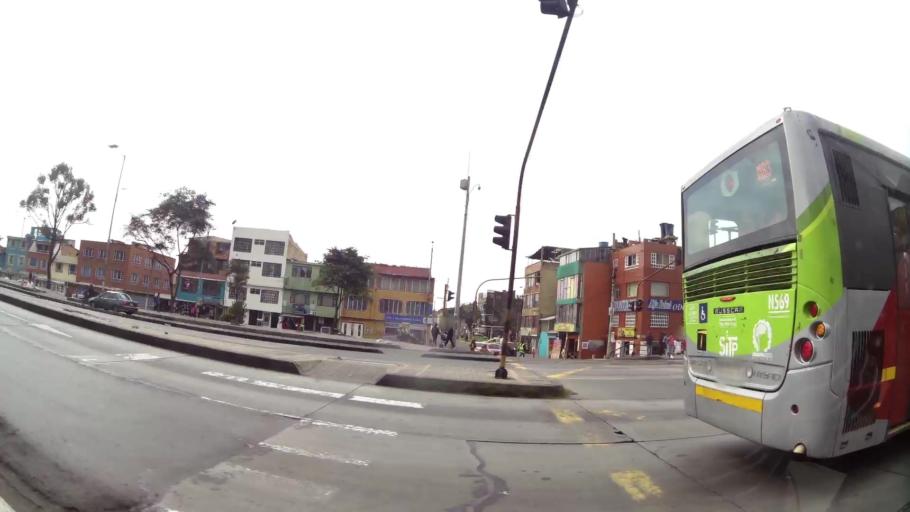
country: CO
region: Bogota D.C.
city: Bogota
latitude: 4.5767
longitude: -74.1149
